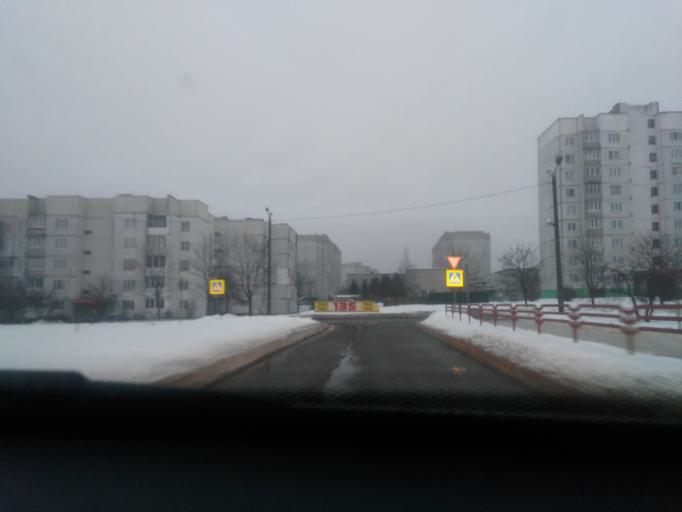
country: BY
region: Mogilev
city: Babruysk
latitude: 53.1991
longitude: 29.2222
